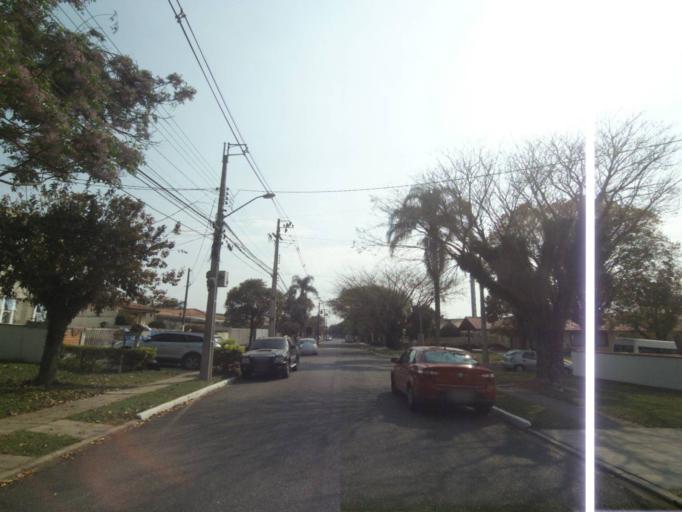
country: BR
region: Parana
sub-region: Pinhais
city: Pinhais
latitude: -25.4797
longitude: -49.2043
